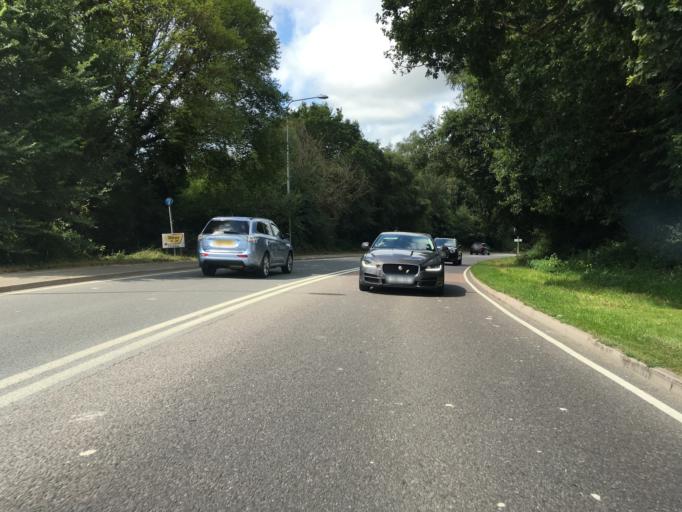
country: GB
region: England
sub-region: East Sussex
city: Pevensey
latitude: 50.8445
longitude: 0.4010
